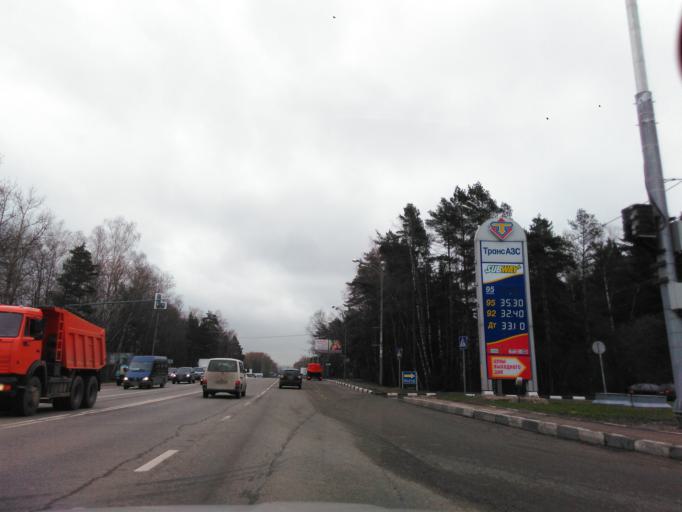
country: RU
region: Moskovskaya
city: Opalikha
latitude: 55.8407
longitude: 37.2216
